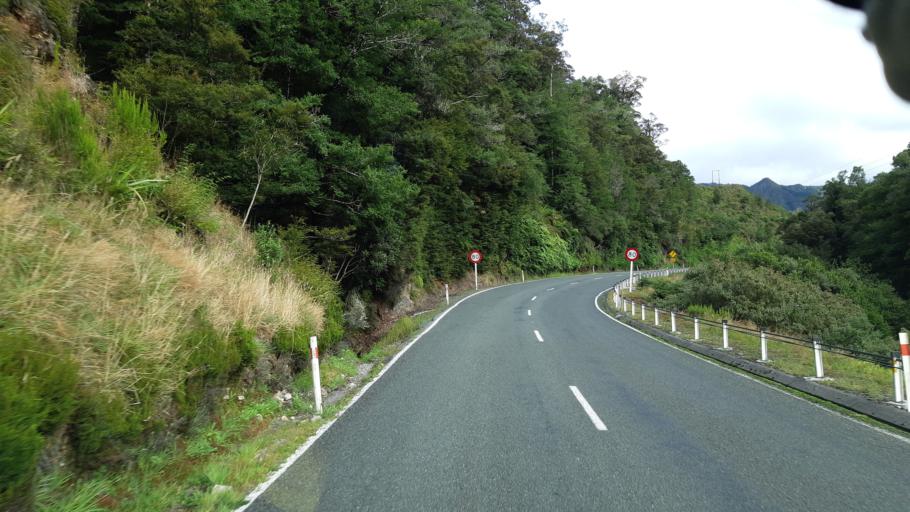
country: NZ
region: West Coast
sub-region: Buller District
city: Westport
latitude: -41.9882
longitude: 172.2125
